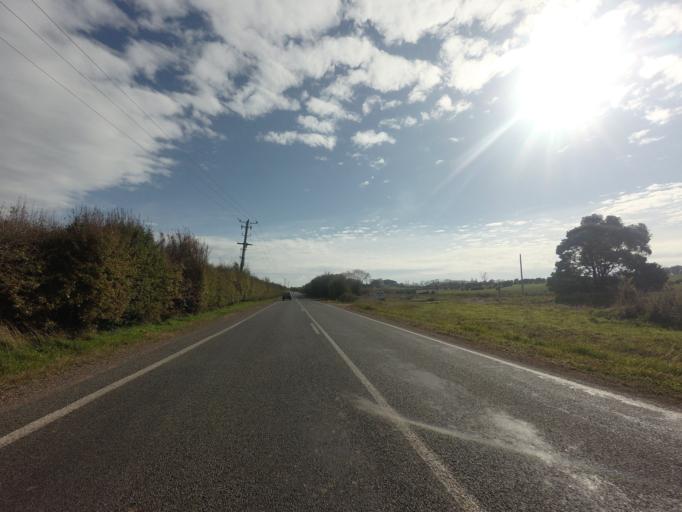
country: AU
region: Tasmania
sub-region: Meander Valley
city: Westbury
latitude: -41.5261
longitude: 146.7891
